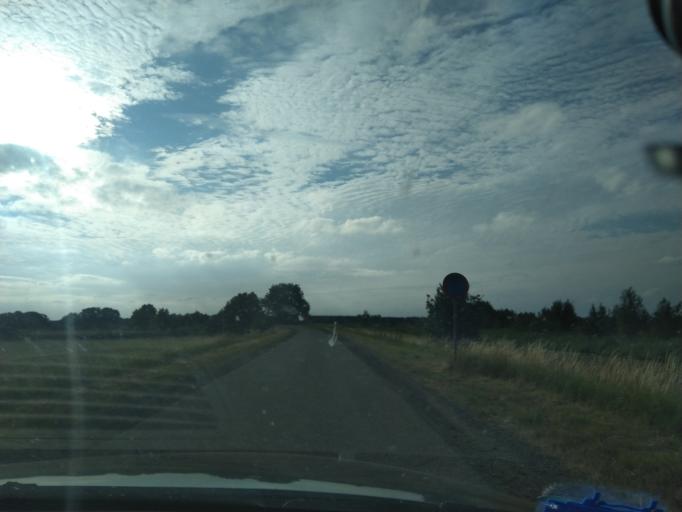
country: NL
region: Groningen
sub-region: Gemeente Vlagtwedde
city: Vlagtwedde
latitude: 53.0919
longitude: 7.0989
